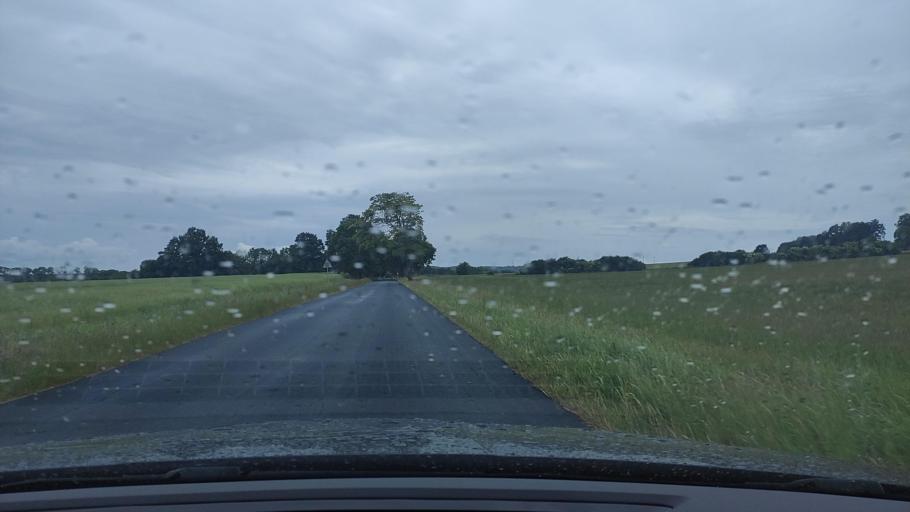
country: PL
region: West Pomeranian Voivodeship
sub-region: Powiat slawienski
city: Slawno
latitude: 54.5181
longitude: 16.5817
